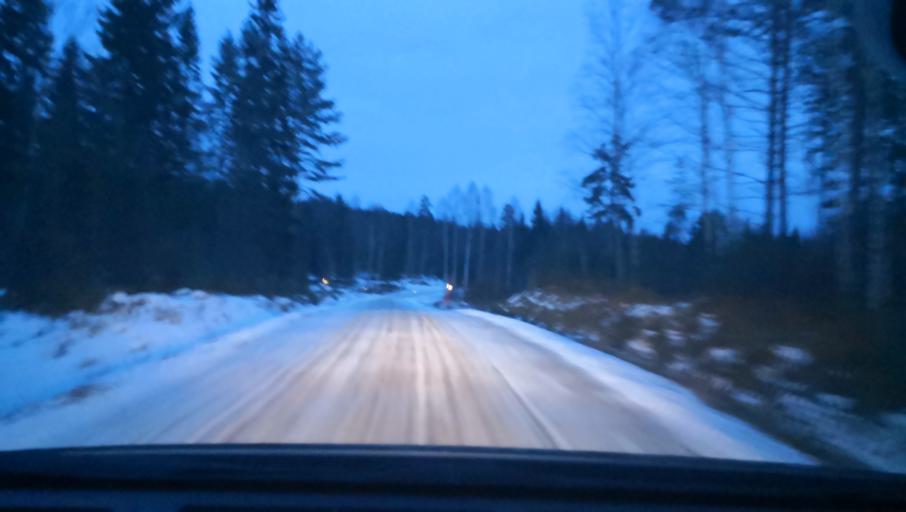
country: SE
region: Dalarna
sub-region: Avesta Kommun
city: Horndal
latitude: 60.2296
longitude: 16.6470
